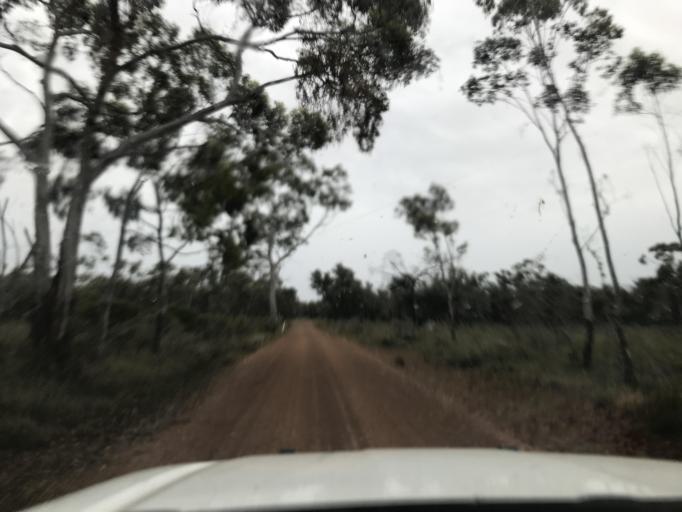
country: AU
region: South Australia
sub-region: Wattle Range
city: Penola
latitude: -37.0935
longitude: 141.5067
